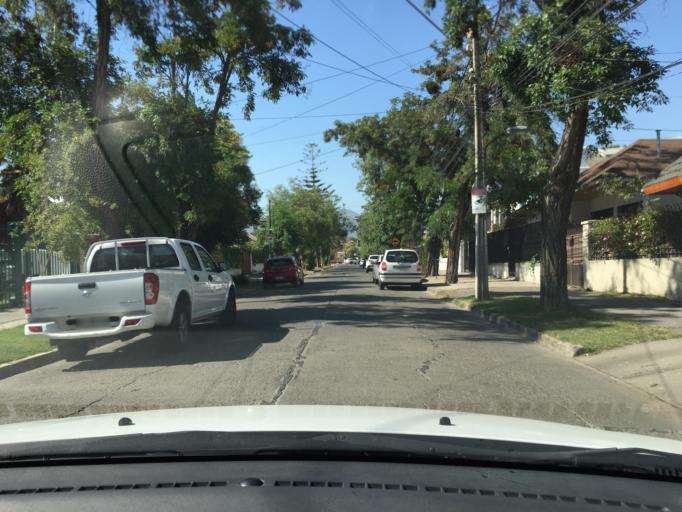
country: CL
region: Santiago Metropolitan
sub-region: Provincia de Santiago
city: Villa Presidente Frei, Nunoa, Santiago, Chile
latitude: -33.4439
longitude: -70.5822
